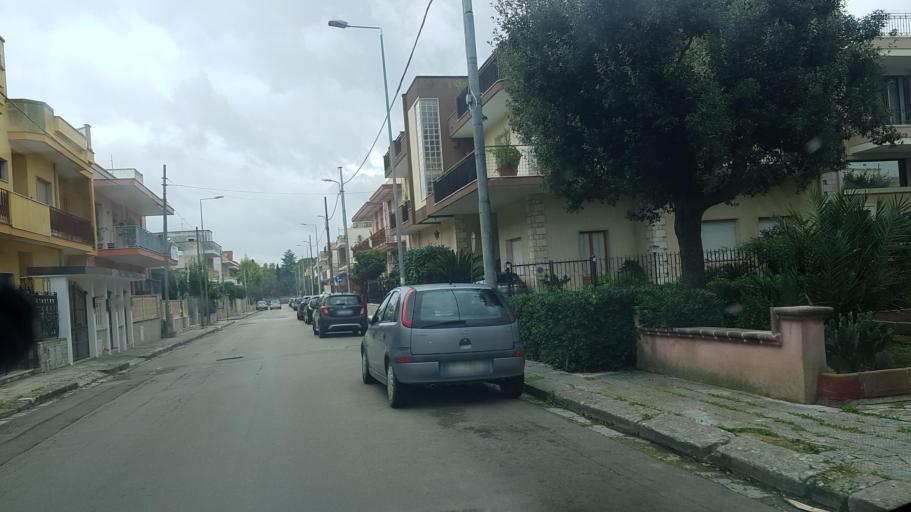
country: IT
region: Apulia
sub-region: Provincia di Lecce
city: Novoli
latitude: 40.3739
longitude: 18.0465
